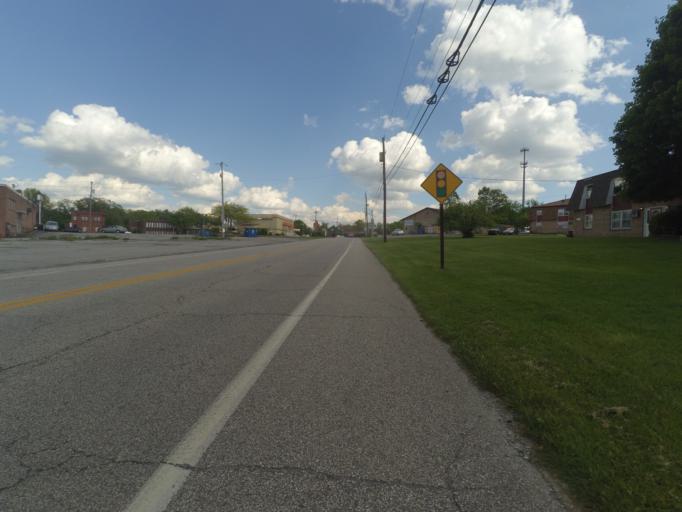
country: US
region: Ohio
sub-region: Mahoning County
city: Boardman
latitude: 41.0475
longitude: -80.6642
